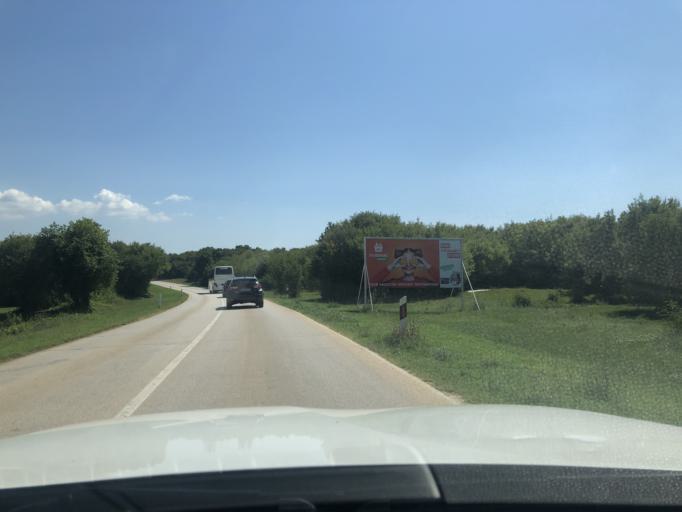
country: HR
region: Istarska
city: Vodnjan
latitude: 45.0374
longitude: 13.7823
